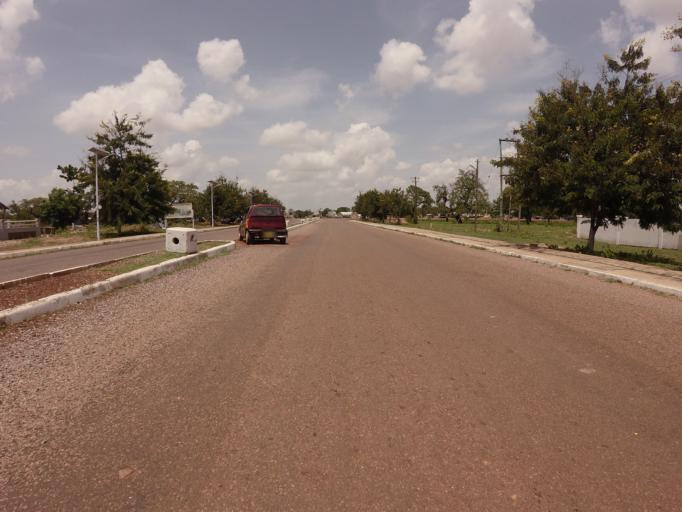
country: GH
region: Northern
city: Tamale
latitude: 9.3688
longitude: -0.8826
